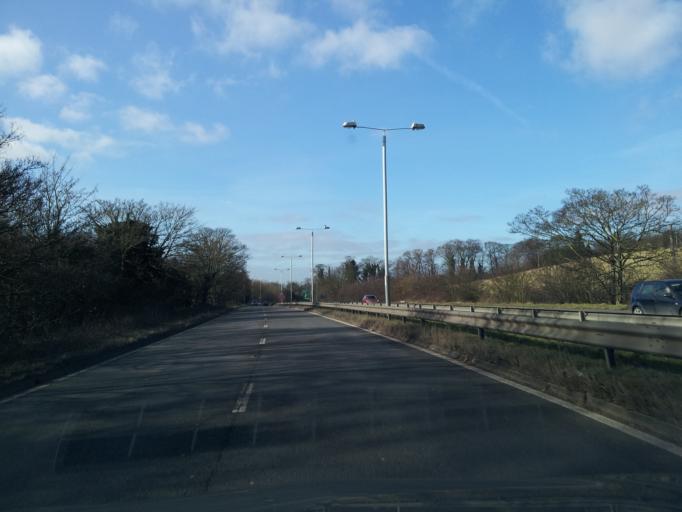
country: GB
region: England
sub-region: Nottinghamshire
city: Ruddington
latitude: 52.9051
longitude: -1.1346
